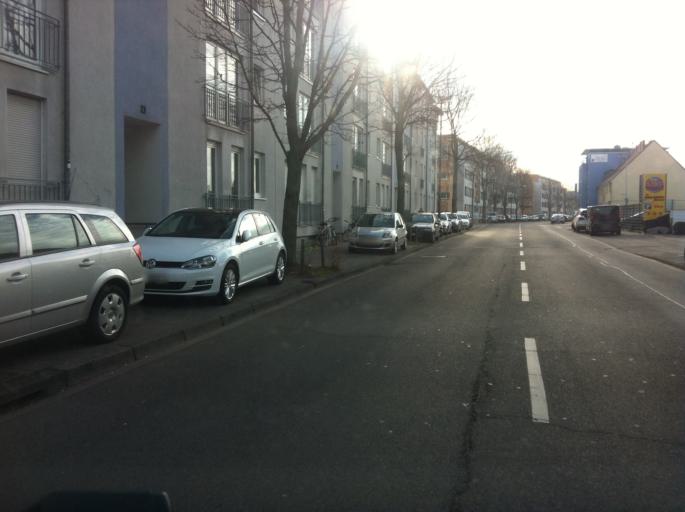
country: DE
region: North Rhine-Westphalia
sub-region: Regierungsbezirk Koln
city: Bilderstoeckchen
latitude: 50.9561
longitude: 6.9000
